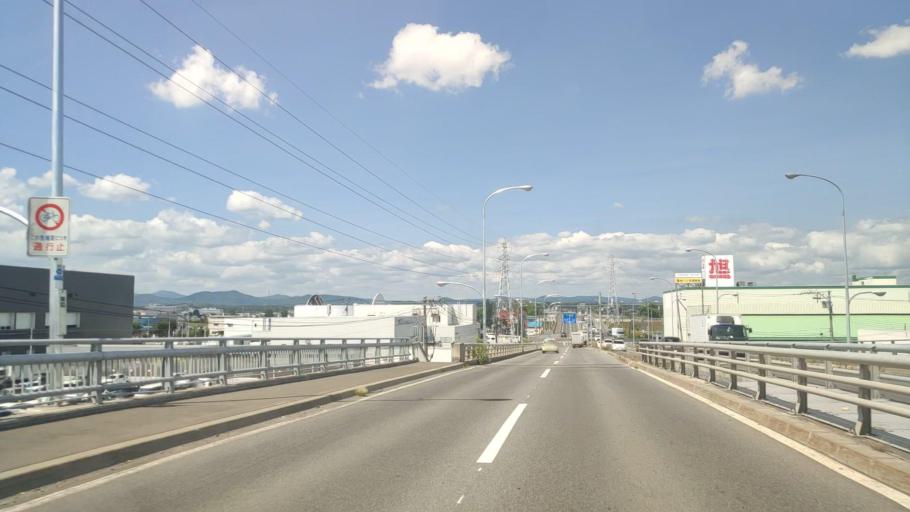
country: JP
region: Hokkaido
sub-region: Asahikawa-shi
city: Asahikawa
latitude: 43.7940
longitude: 142.4006
